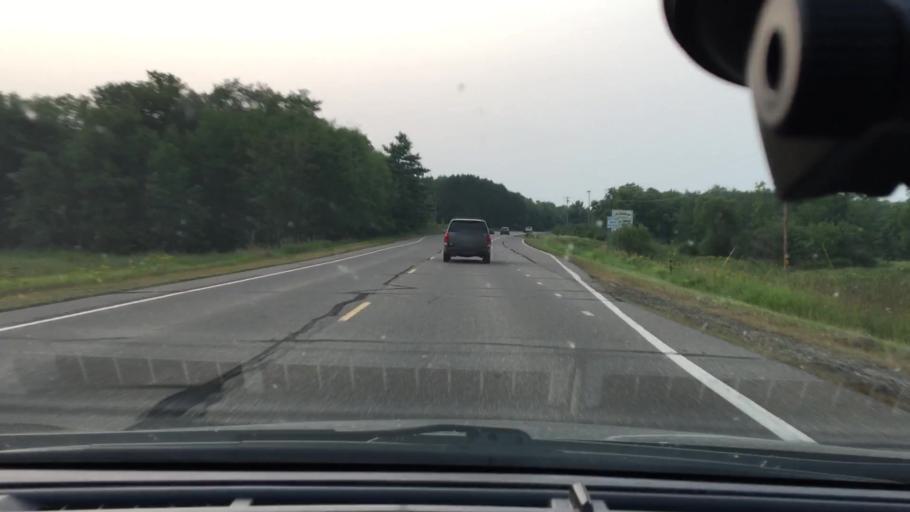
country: US
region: Minnesota
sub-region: Crow Wing County
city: Crosby
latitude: 46.4575
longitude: -93.8828
